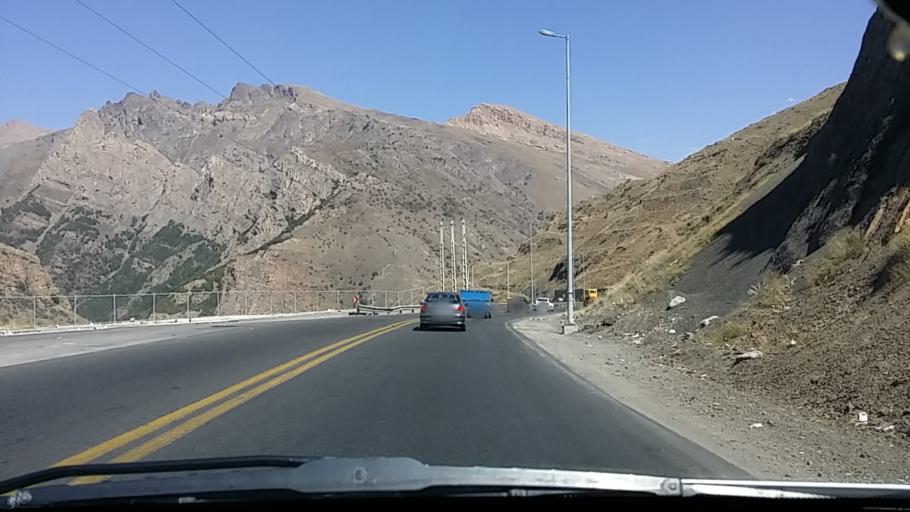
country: IR
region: Tehran
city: Tajrish
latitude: 36.1971
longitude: 51.3226
